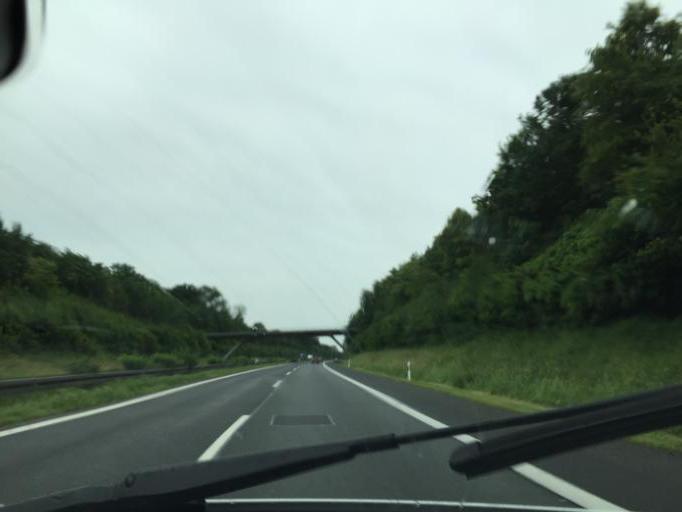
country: DE
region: Bavaria
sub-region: Regierungsbezirk Unterfranken
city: Hassfurt
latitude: 50.0043
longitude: 10.5040
